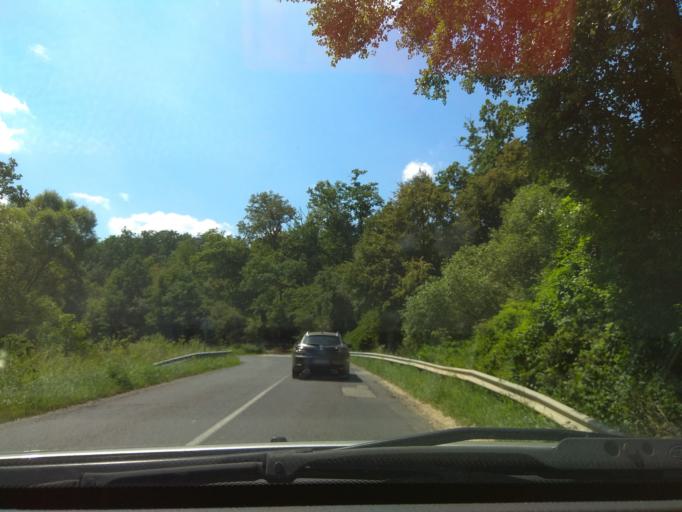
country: HU
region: Borsod-Abauj-Zemplen
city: Harsany
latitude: 48.0129
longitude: 20.7633
